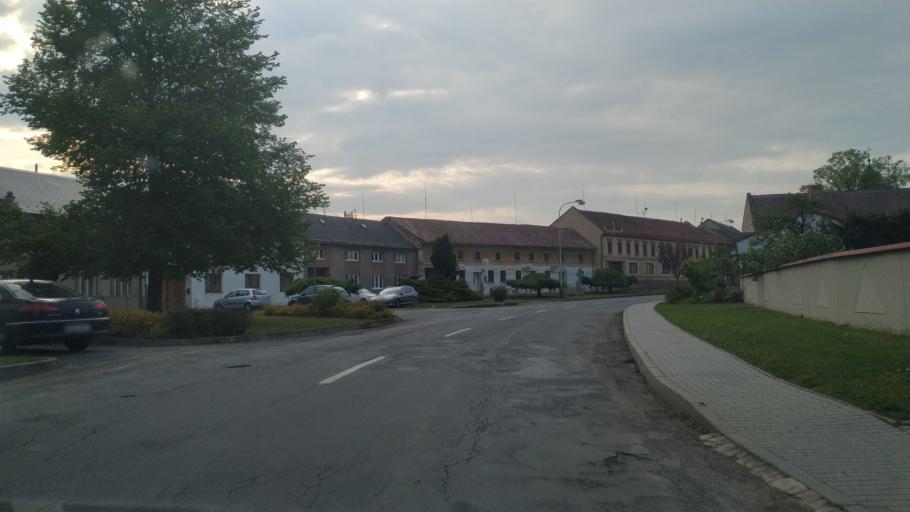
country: CZ
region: Olomoucky
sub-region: Okres Olomouc
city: Slatinice
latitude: 49.5487
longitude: 17.1152
